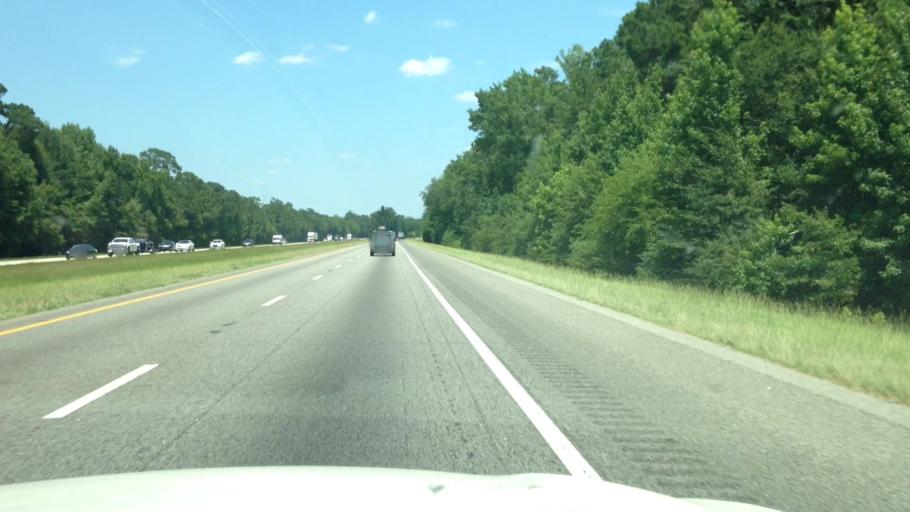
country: US
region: South Carolina
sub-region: Dillon County
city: Latta
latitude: 34.3972
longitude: -79.4527
